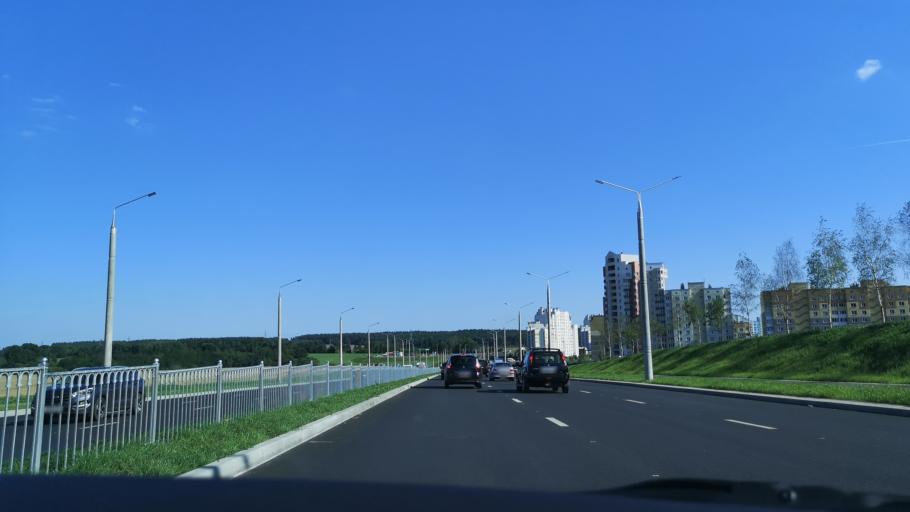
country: BY
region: Grodnenskaya
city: Hrodna
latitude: 53.6487
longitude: 23.8632
